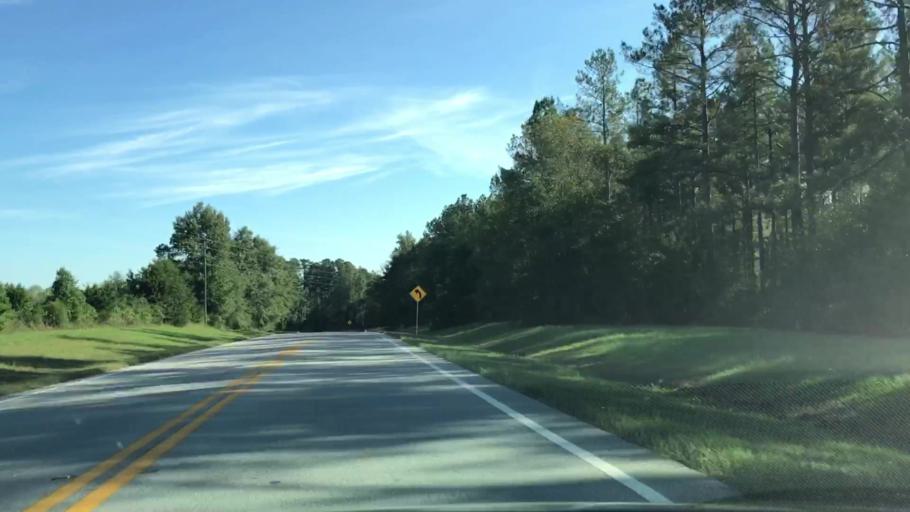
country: US
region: Georgia
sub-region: Glascock County
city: Gibson
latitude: 33.3242
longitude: -82.5589
